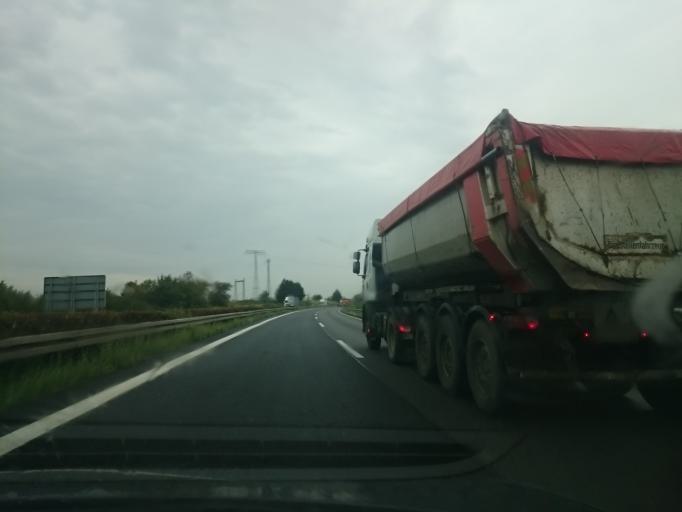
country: DE
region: Brandenburg
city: Wustermark
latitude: 52.4813
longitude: 12.9622
